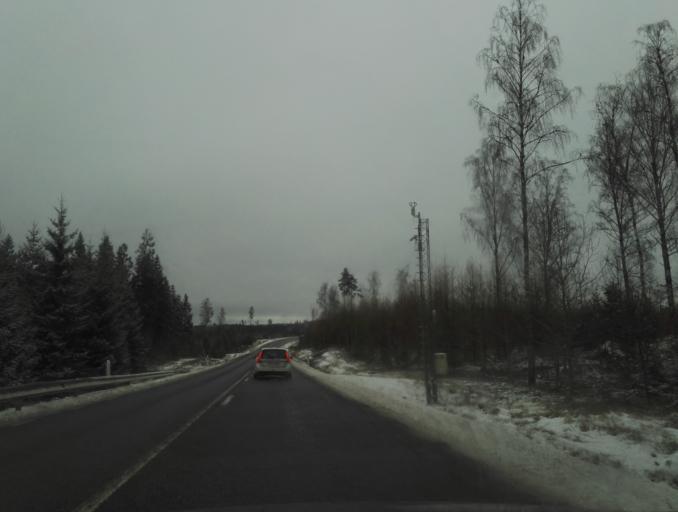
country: SE
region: Kronoberg
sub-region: Vaxjo Kommun
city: Gemla
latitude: 56.8254
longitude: 14.6912
